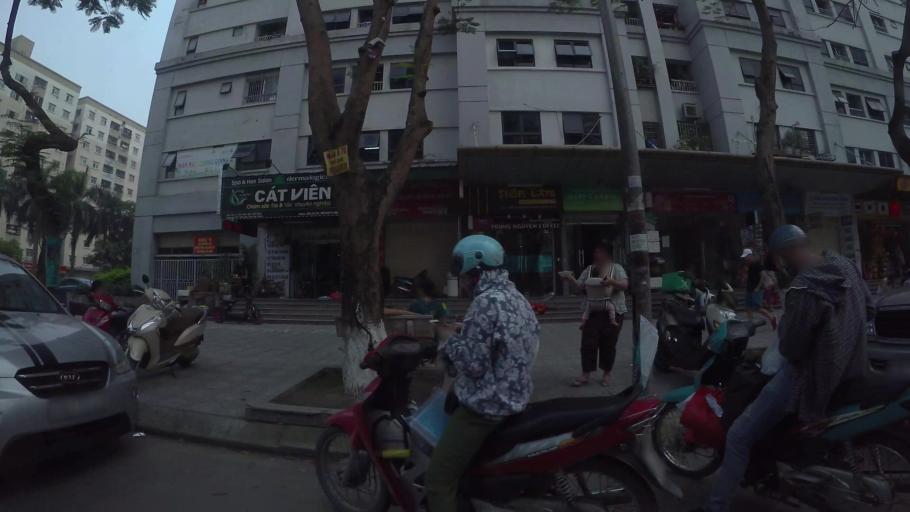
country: VN
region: Ha Noi
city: Van Dien
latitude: 20.9642
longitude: 105.8312
